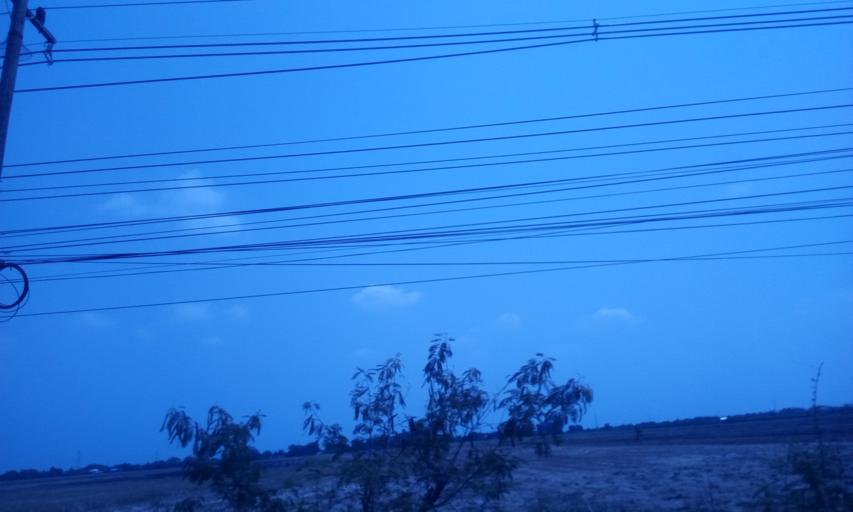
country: TH
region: Chachoengsao
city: Bang Nam Priao
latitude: 13.8113
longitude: 101.0535
